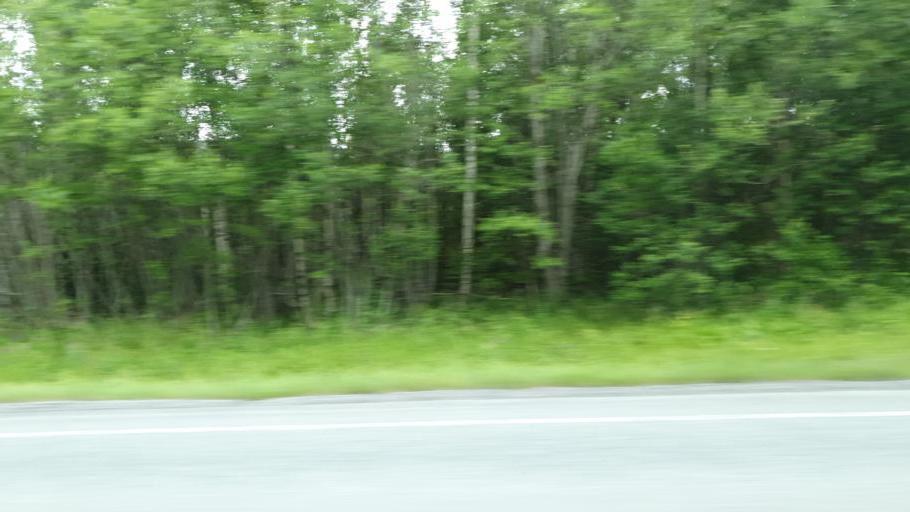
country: NO
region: Sor-Trondelag
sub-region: Rennebu
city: Berkak
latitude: 62.7883
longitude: 10.0025
